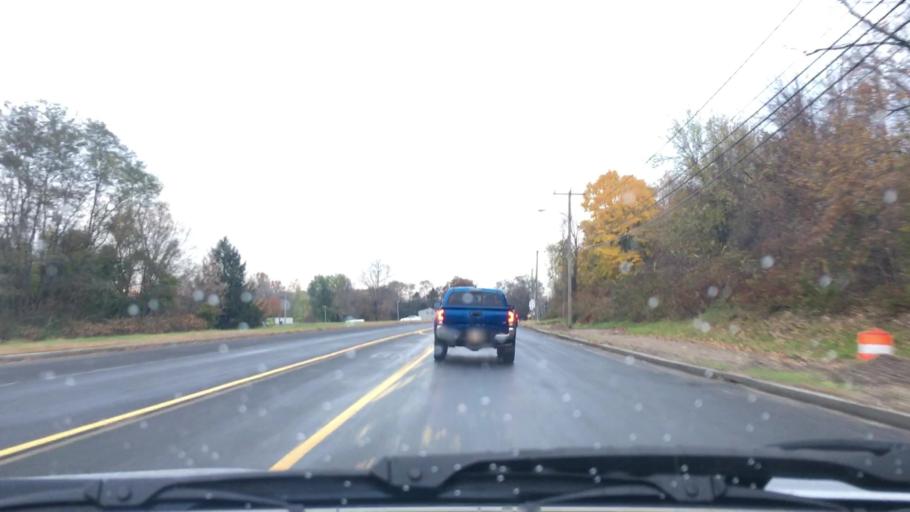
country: US
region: Massachusetts
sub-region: Hampden County
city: Agawam
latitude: 42.0570
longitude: -72.6757
